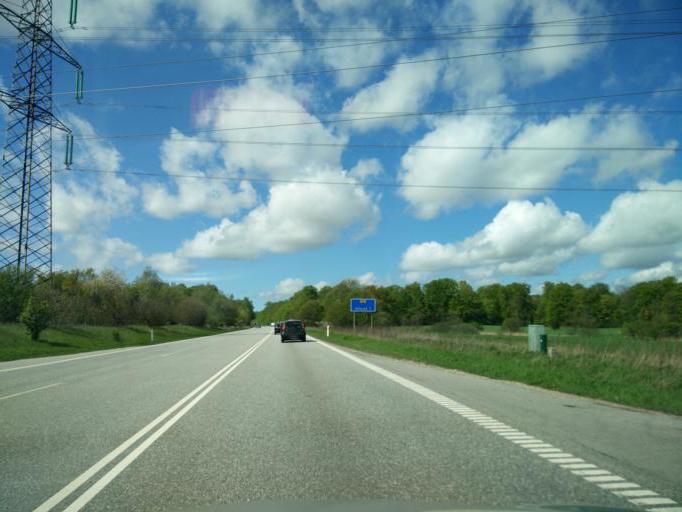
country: DK
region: Capital Region
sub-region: Allerod Kommune
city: Lillerod
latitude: 55.8827
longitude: 12.3018
